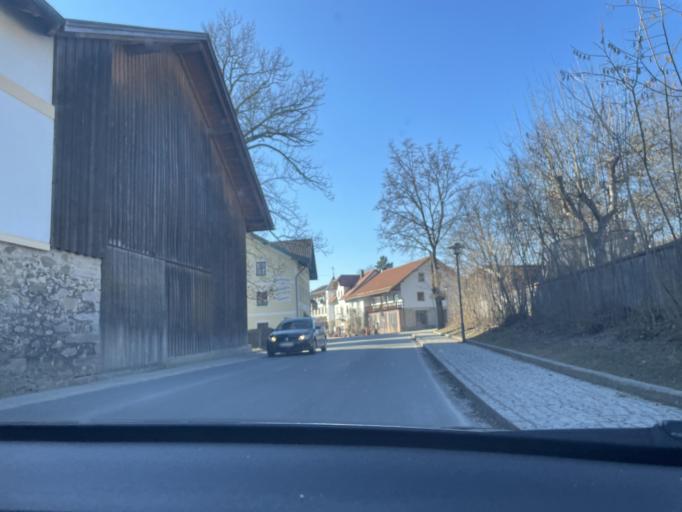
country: DE
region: Bavaria
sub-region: Lower Bavaria
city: Arnbruck
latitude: 49.1293
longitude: 12.9964
